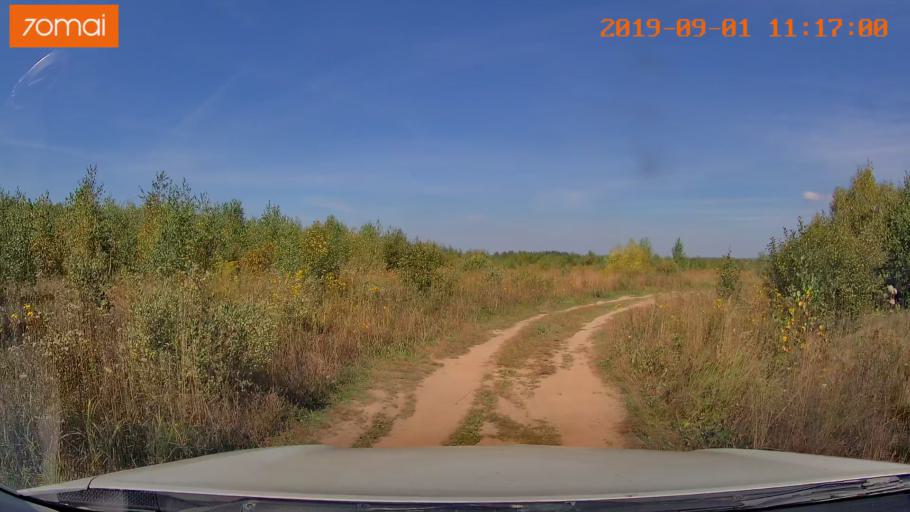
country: RU
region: Kaluga
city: Detchino
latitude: 54.8244
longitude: 36.3674
